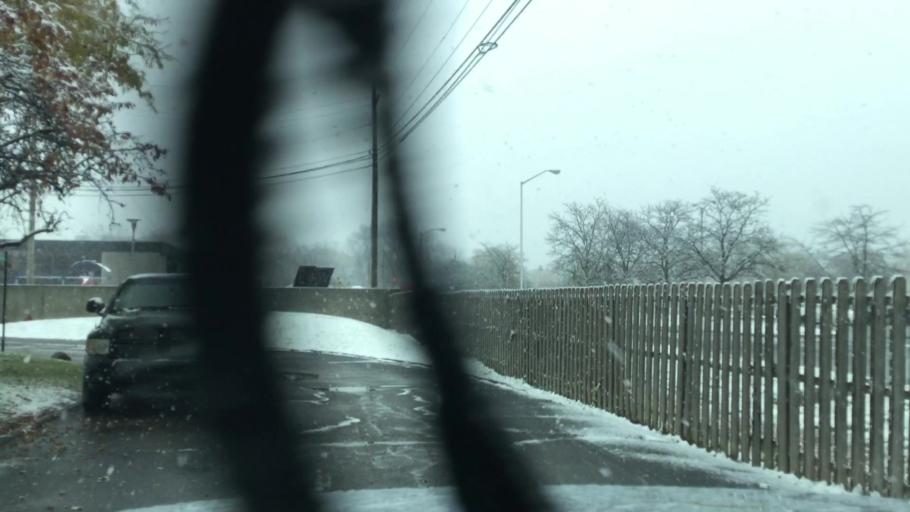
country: US
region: Michigan
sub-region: Oakland County
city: Southfield
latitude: 42.4651
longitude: -83.2235
